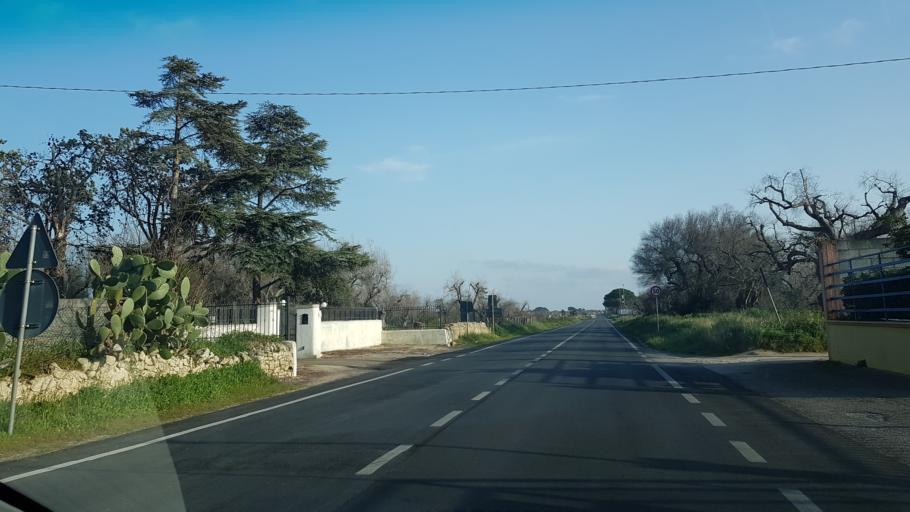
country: IT
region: Apulia
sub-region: Provincia di Lecce
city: Squinzano
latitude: 40.4257
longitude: 18.0546
